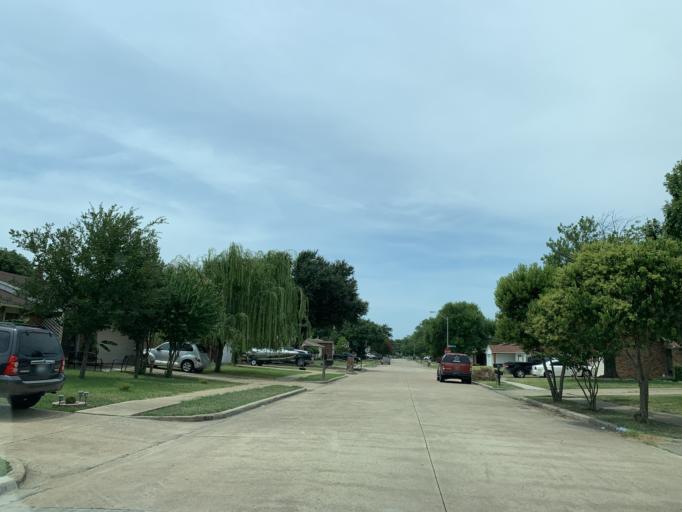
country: US
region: Texas
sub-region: Dallas County
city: Grand Prairie
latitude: 32.6562
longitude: -97.0239
